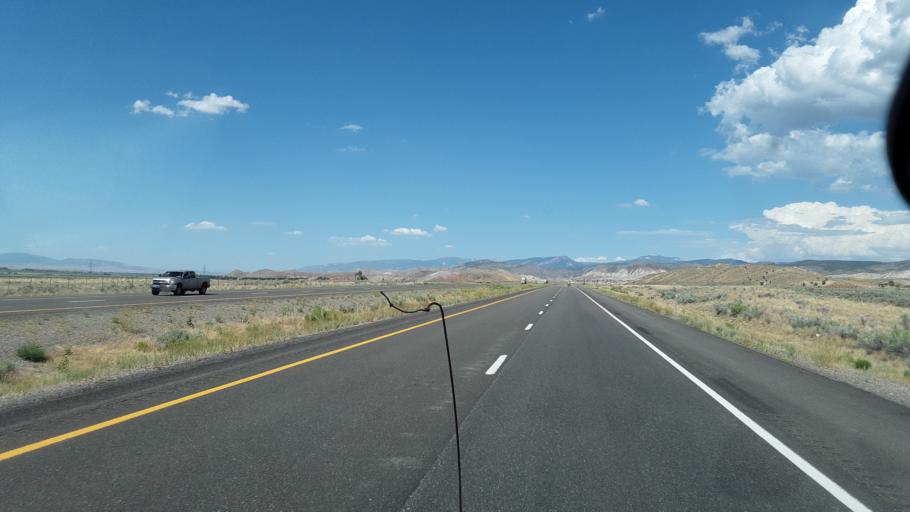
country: US
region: Utah
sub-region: Sevier County
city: Aurora
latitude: 38.8827
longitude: -111.9211
